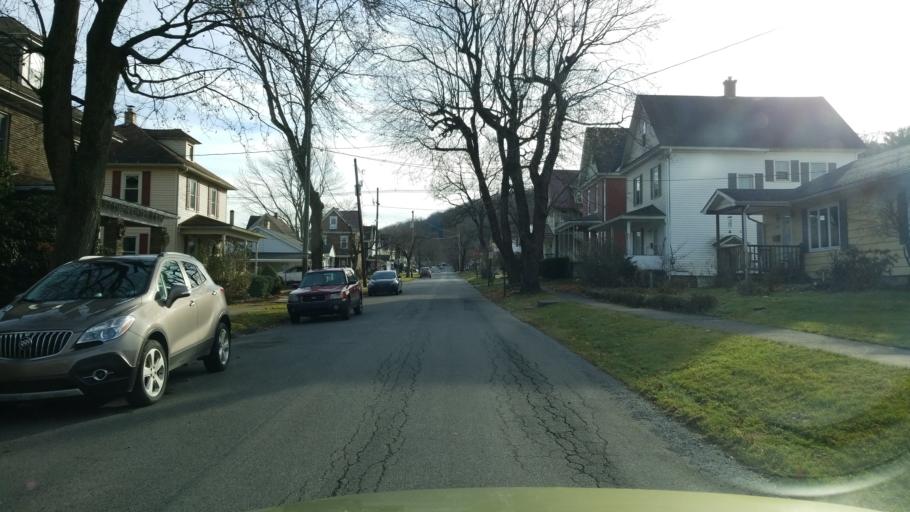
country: US
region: Pennsylvania
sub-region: Clearfield County
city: Clearfield
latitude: 41.0264
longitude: -78.4484
